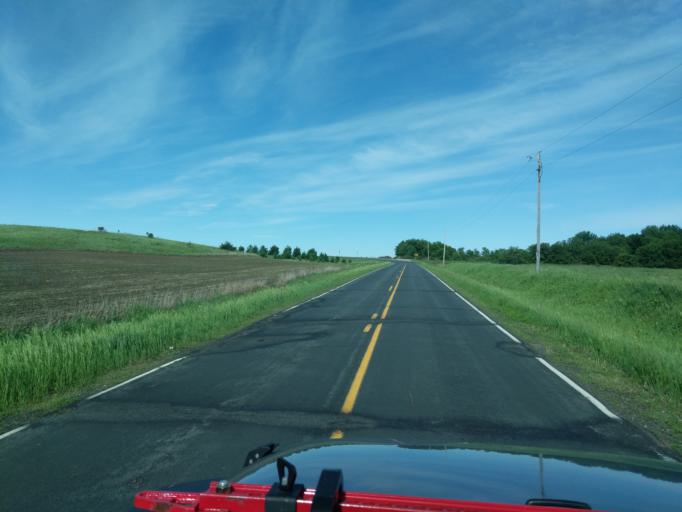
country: US
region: Wisconsin
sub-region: Saint Croix County
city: Hammond
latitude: 44.8806
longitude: -92.4937
